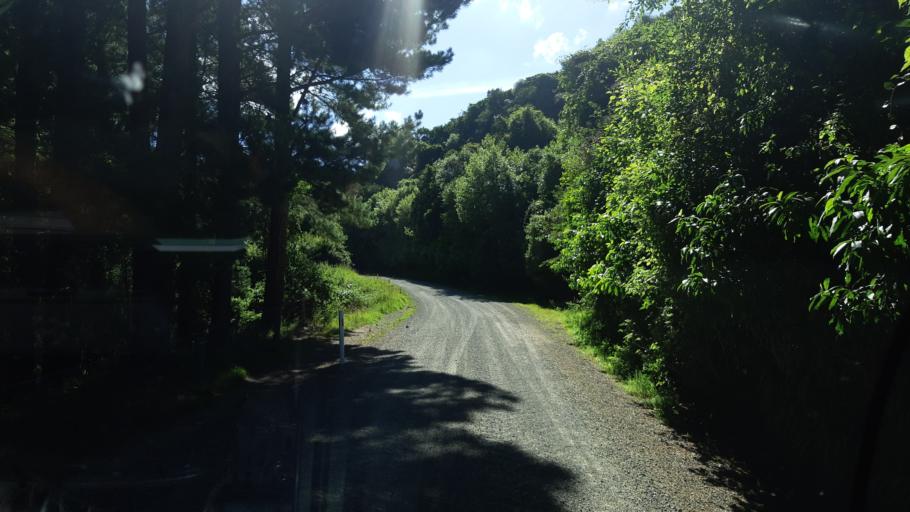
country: NZ
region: Canterbury
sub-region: Timaru District
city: Pleasant Point
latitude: -44.3291
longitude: 170.8686
